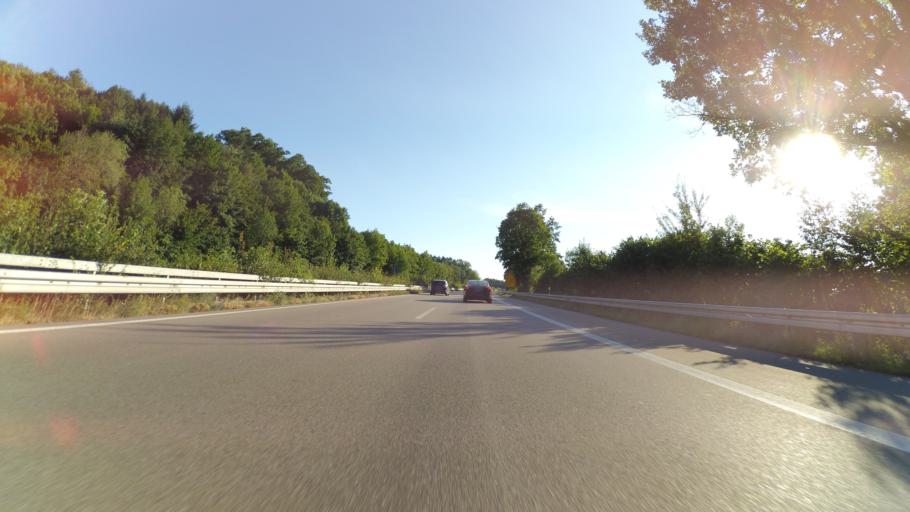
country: DE
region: Baden-Wuerttemberg
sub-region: Freiburg Region
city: Sexau
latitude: 48.0753
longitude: 7.9230
